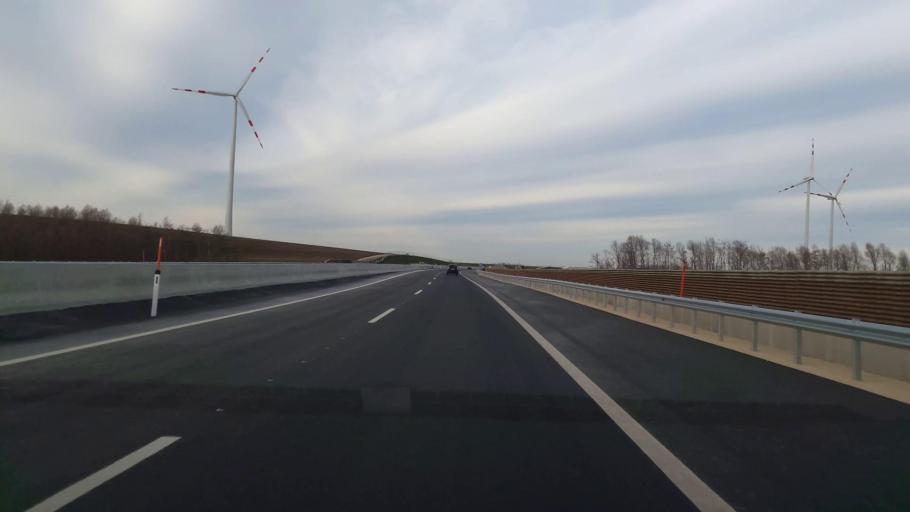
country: AT
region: Lower Austria
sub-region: Politischer Bezirk Mistelbach
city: Grosskrut
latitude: 48.6201
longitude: 16.6765
